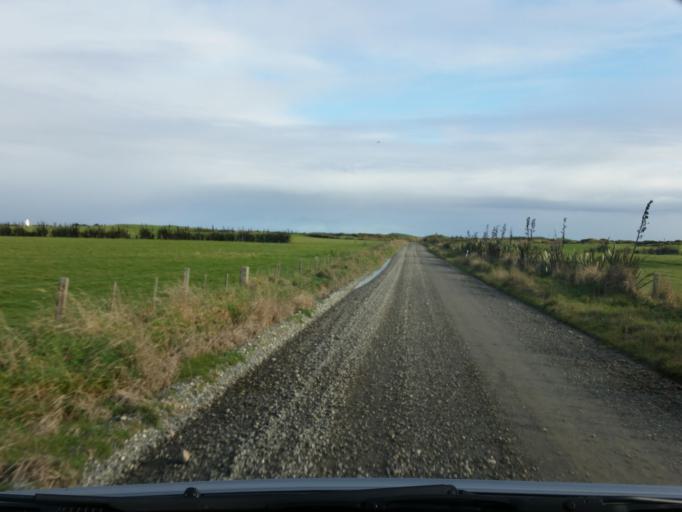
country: NZ
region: Southland
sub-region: Invercargill City
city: Bluff
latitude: -46.6549
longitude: 168.8622
